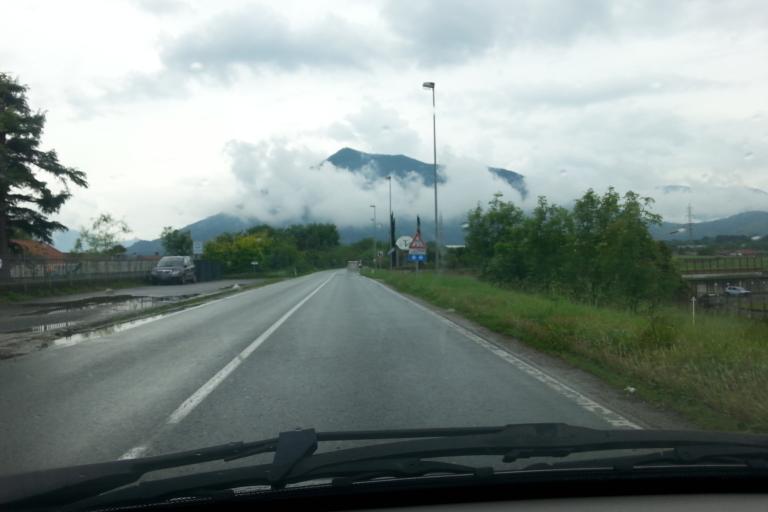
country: IT
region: Piedmont
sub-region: Provincia di Torino
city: Alpignano
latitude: 45.1032
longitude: 7.5083
